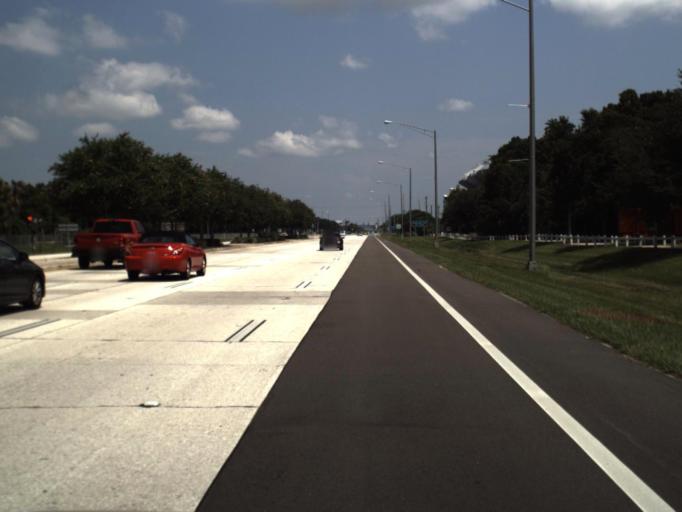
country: US
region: Florida
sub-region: Hillsborough County
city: Egypt Lake-Leto
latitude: 27.9688
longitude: -82.5053
